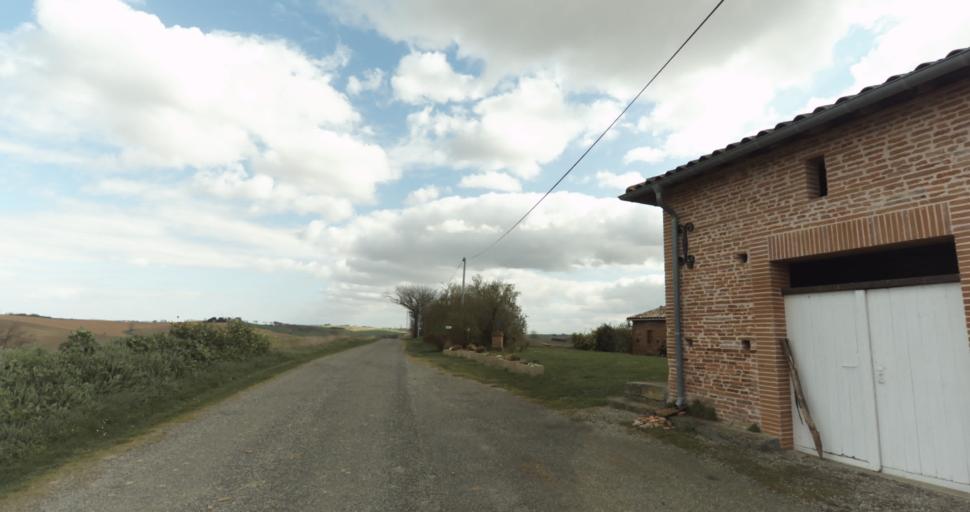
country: FR
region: Midi-Pyrenees
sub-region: Departement de la Haute-Garonne
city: Auterive
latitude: 43.3643
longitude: 1.4917
